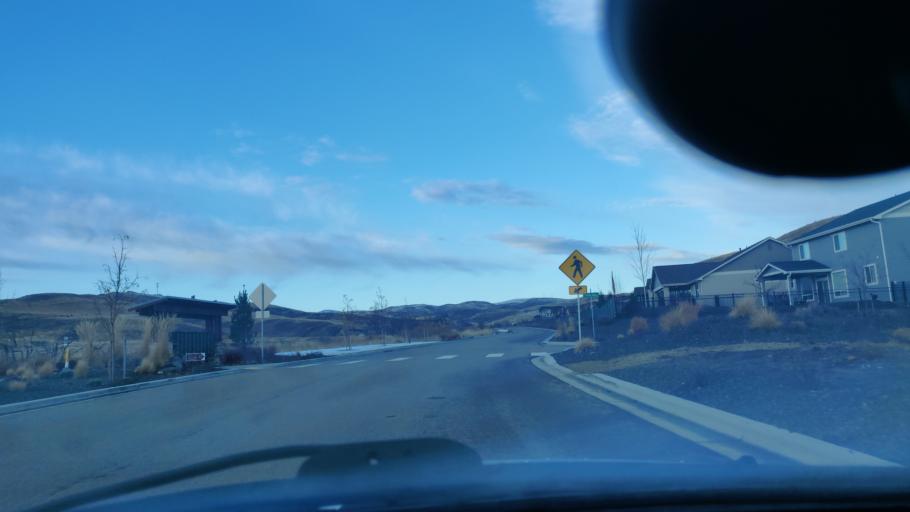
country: US
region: Idaho
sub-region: Ada County
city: Eagle
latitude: 43.7777
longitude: -116.2624
